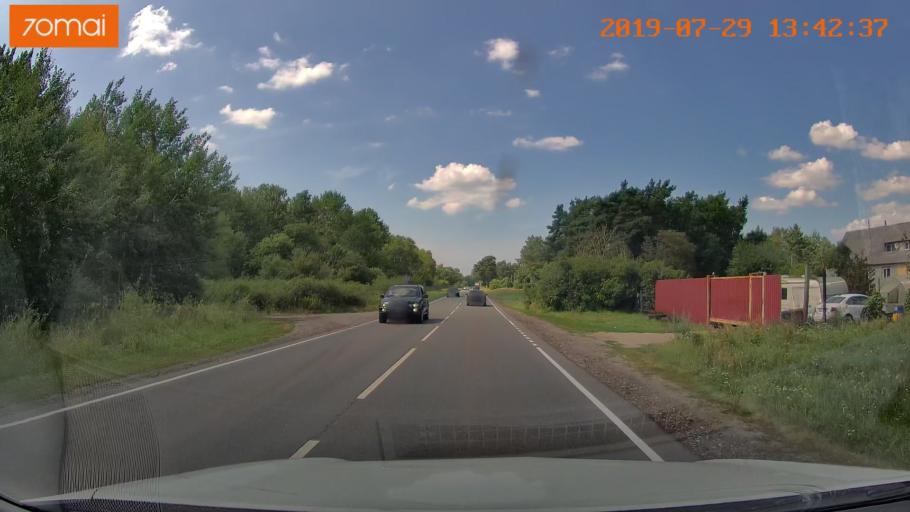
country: RU
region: Kaliningrad
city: Svetlyy
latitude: 54.7368
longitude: 20.1090
